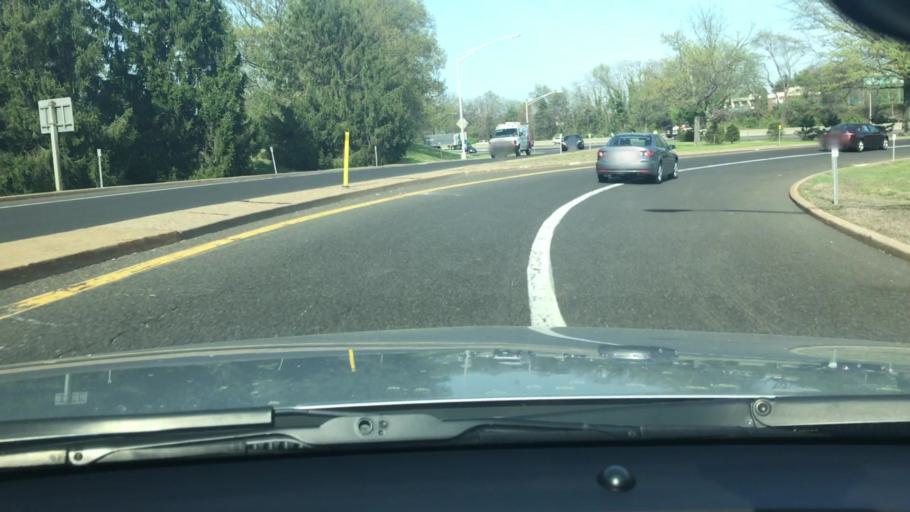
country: US
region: New Jersey
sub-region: Burlington County
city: Willingboro
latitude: 40.0271
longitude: -74.8230
